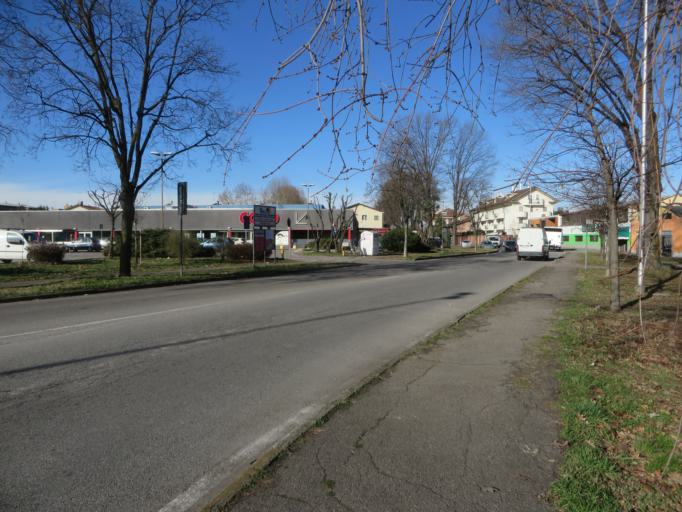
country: IT
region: Lombardy
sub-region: Citta metropolitana di Milano
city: Bareggio
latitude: 45.4859
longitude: 8.9974
